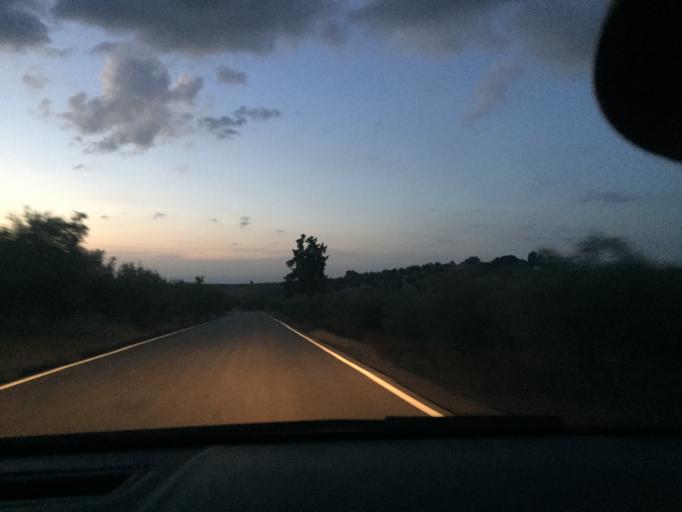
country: ES
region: Andalusia
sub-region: Provincia de Jaen
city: Mancha Real
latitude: 37.7941
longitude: -3.6457
